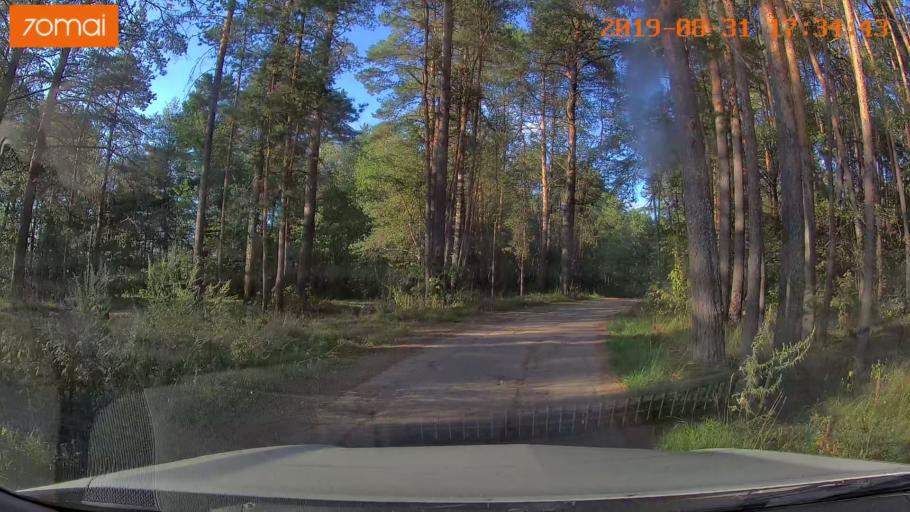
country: RU
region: Kaluga
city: Detchino
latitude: 54.8138
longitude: 36.3521
